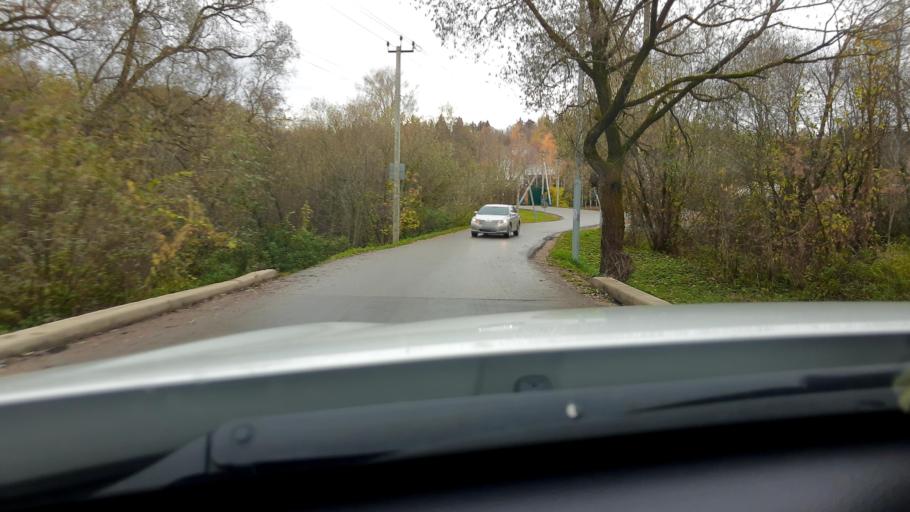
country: RU
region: Moskovskaya
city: Annino
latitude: 55.5609
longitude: 37.2379
